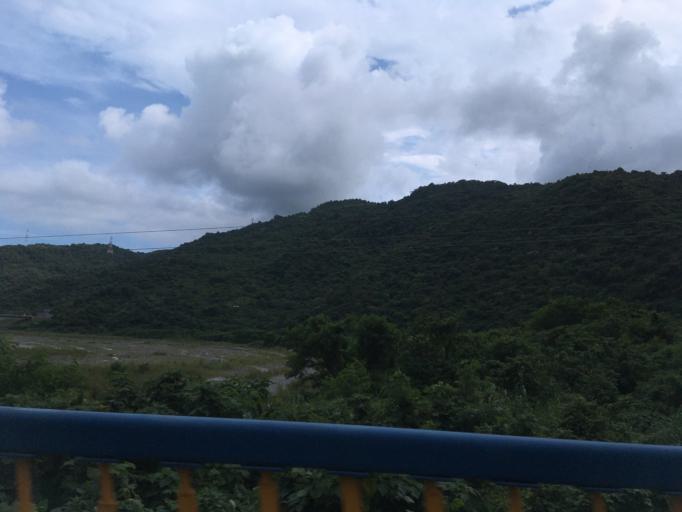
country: TW
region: Taiwan
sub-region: Yilan
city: Yilan
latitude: 24.4437
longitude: 121.7674
